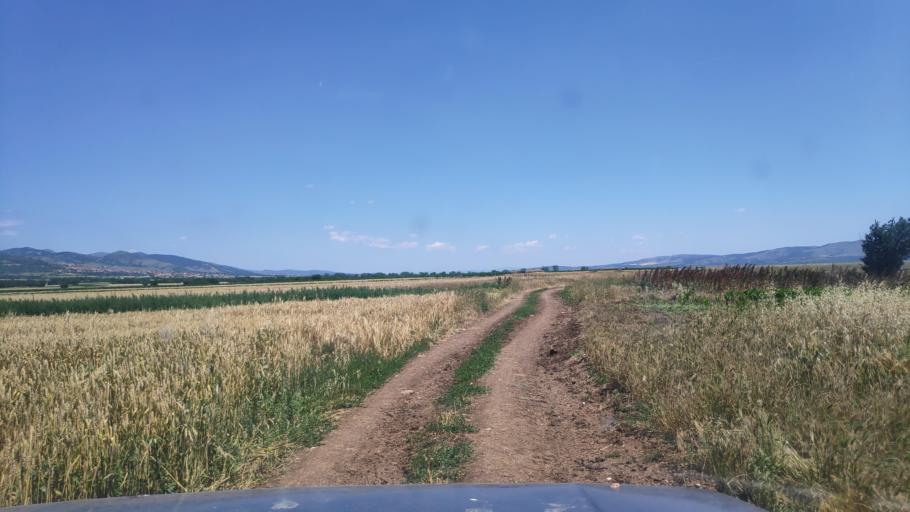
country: MK
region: Kumanovo
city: Bedinje
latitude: 42.1624
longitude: 21.6833
